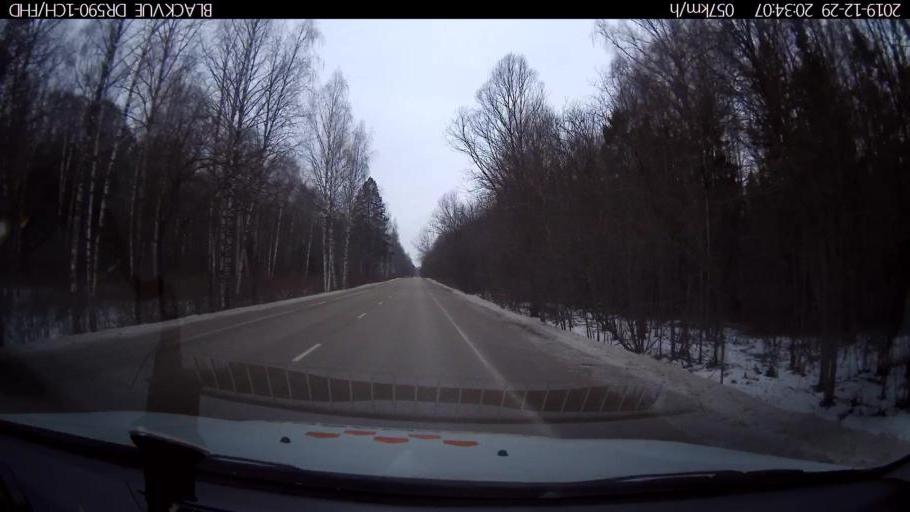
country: RU
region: Nizjnij Novgorod
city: Afonino
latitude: 56.1843
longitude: 44.0434
